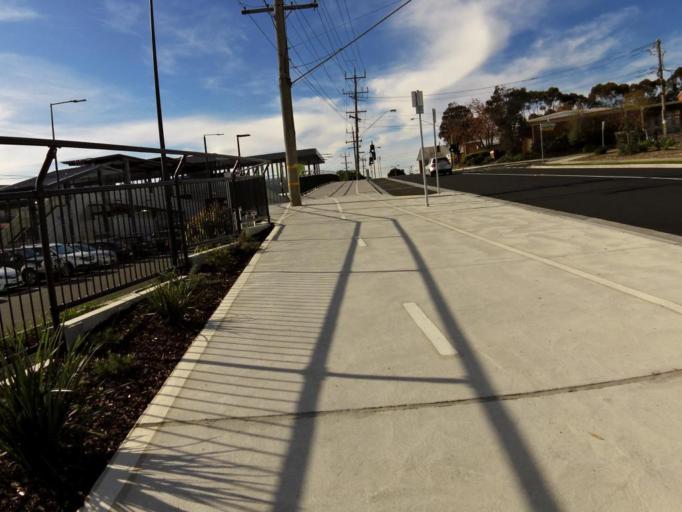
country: AU
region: Victoria
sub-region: Maroondah
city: Ringwood East
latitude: -37.8164
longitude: 145.2288
